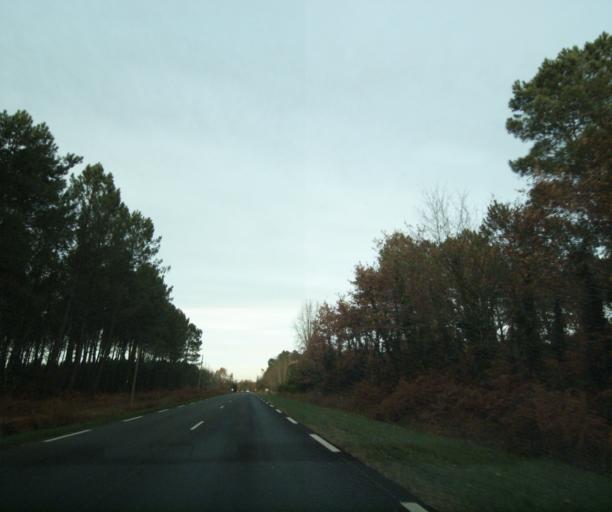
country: FR
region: Aquitaine
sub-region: Departement de la Gironde
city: Bazas
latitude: 44.3326
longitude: -0.2366
